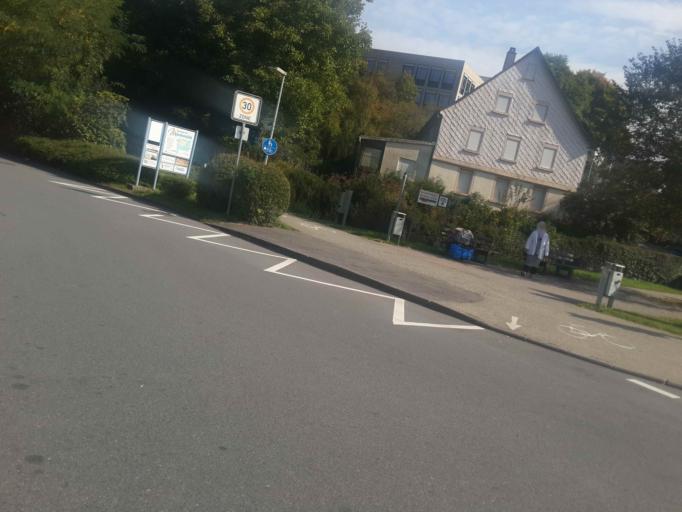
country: DE
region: Baden-Wuerttemberg
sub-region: Regierungsbezirk Stuttgart
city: Mockmuhl
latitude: 49.3216
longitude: 9.3645
